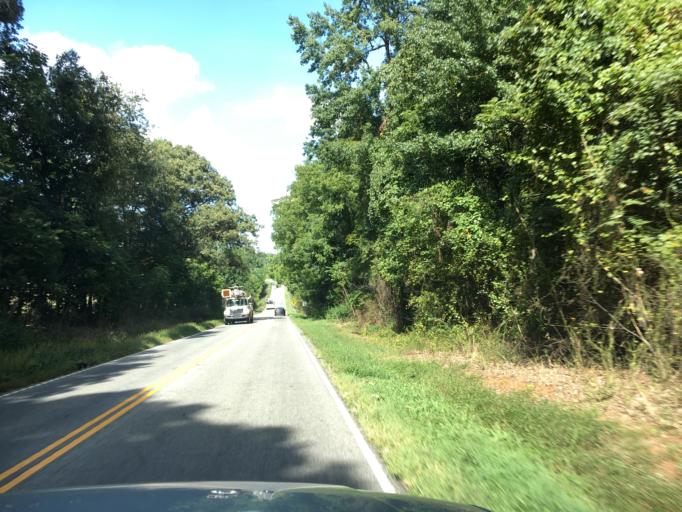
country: US
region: South Carolina
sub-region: Spartanburg County
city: Inman Mills
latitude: 35.0333
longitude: -82.0971
